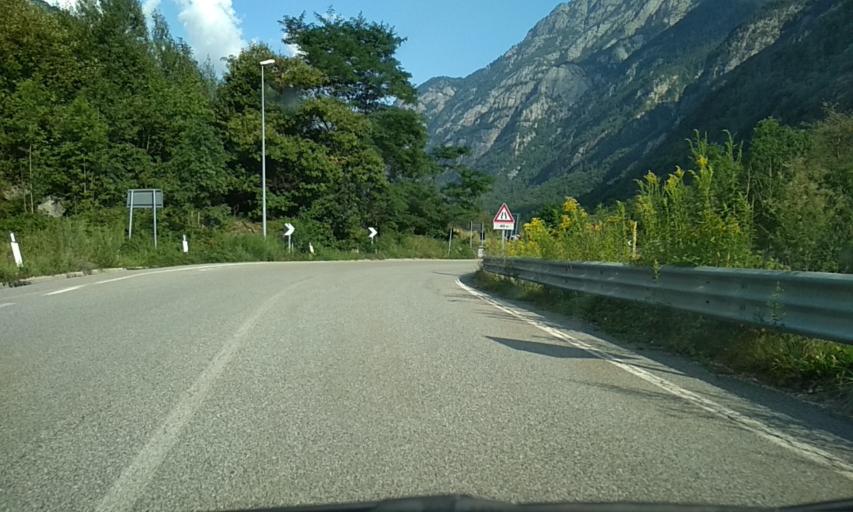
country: IT
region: Piedmont
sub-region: Provincia di Torino
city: Noasca
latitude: 45.4332
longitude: 7.3608
